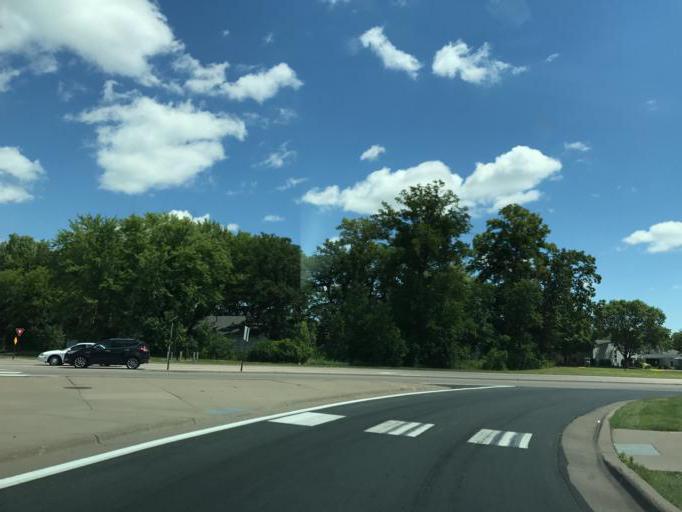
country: US
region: Minnesota
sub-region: Hennepin County
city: Maple Grove
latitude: 45.0811
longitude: -93.4783
